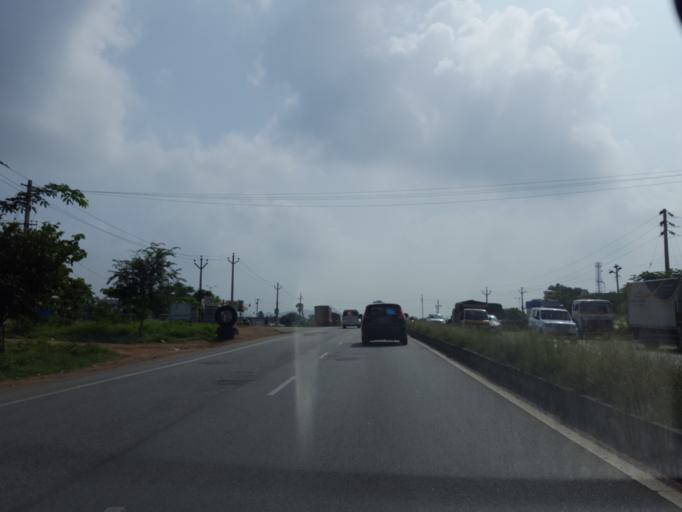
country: IN
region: Telangana
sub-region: Rangareddi
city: Ghatkesar
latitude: 17.2931
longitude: 78.7500
